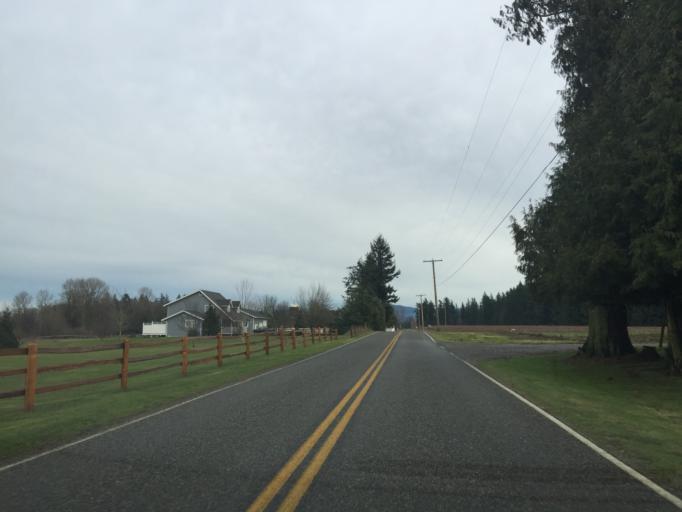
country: US
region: Washington
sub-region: Whatcom County
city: Ferndale
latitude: 48.8988
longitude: -122.5336
